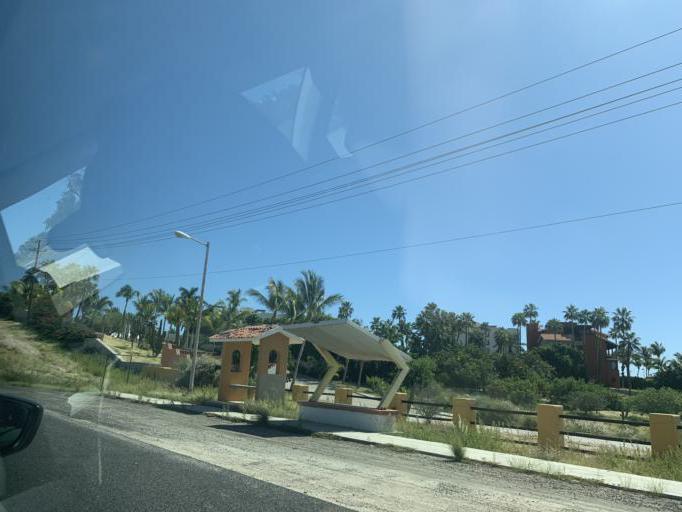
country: MX
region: Baja California Sur
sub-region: Los Cabos
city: San Jose del Cabo
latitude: 22.9791
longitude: -109.7726
